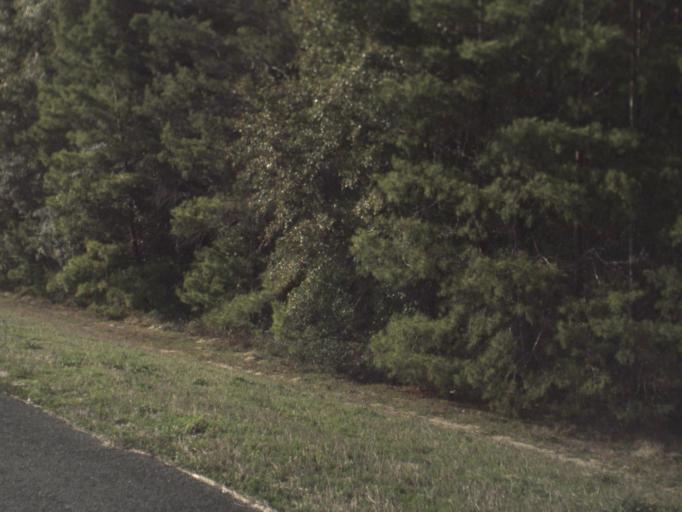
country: US
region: Florida
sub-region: Bay County
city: Youngstown
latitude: 30.4277
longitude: -85.5773
